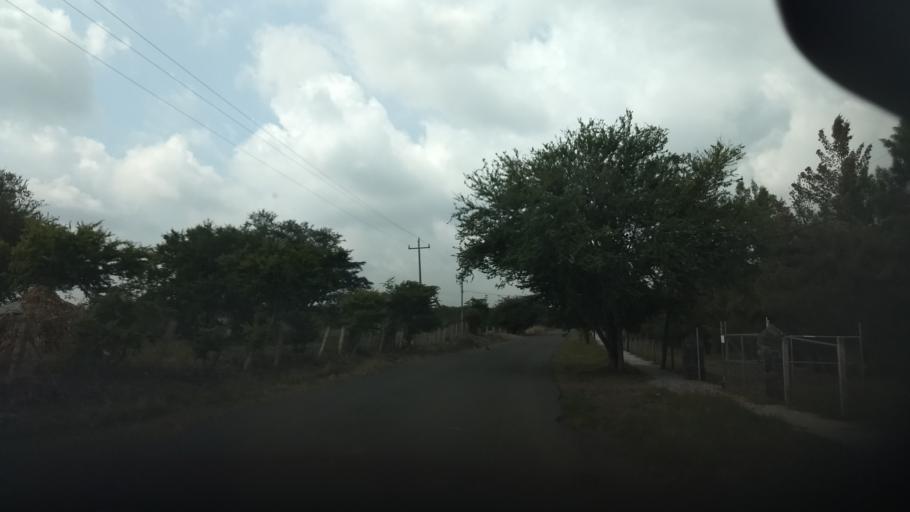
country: MX
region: Jalisco
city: Tonila
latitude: 19.3962
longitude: -103.5318
